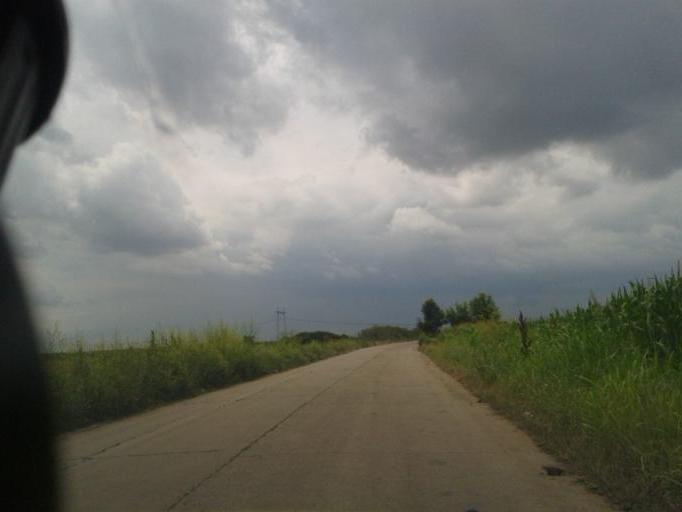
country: RO
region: Calarasi
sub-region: Comuna Fundulea
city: Fundulea
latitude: 44.4873
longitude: 26.5146
